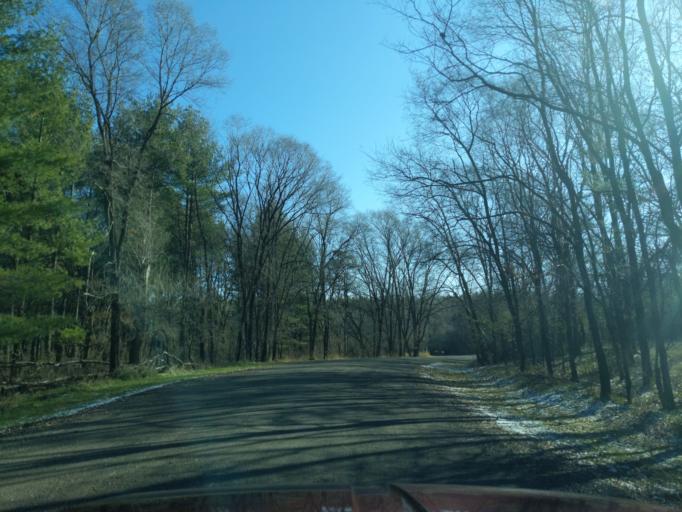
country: US
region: Wisconsin
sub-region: Waushara County
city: Silver Lake
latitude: 44.1212
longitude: -89.1757
